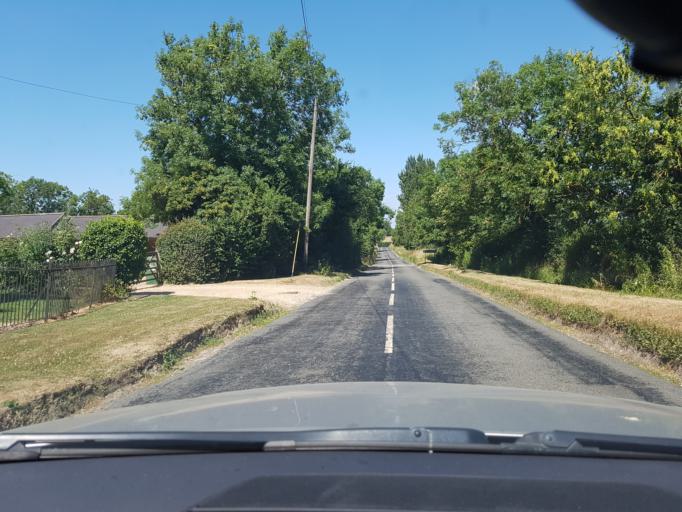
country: GB
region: England
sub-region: Milton Keynes
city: Calverton
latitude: 52.0392
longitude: -0.8441
